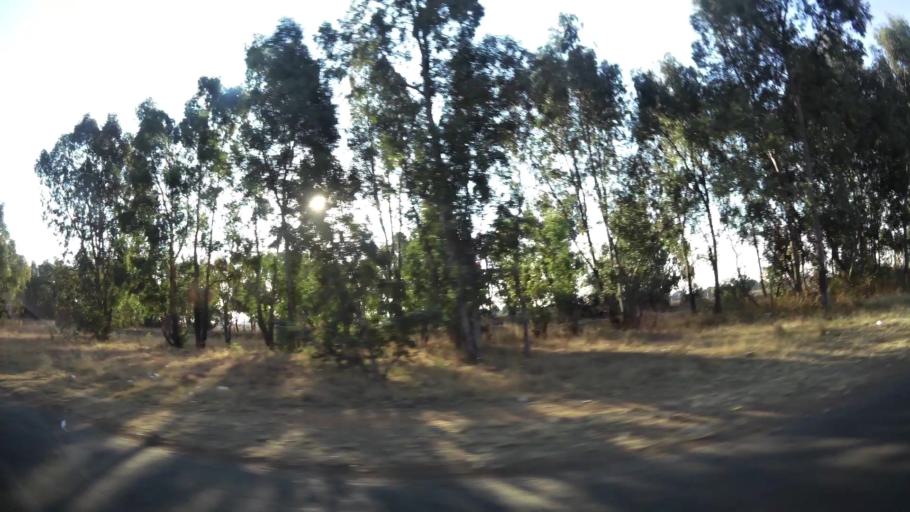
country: ZA
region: Gauteng
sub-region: West Rand District Municipality
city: Randfontein
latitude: -26.1943
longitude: 27.6816
